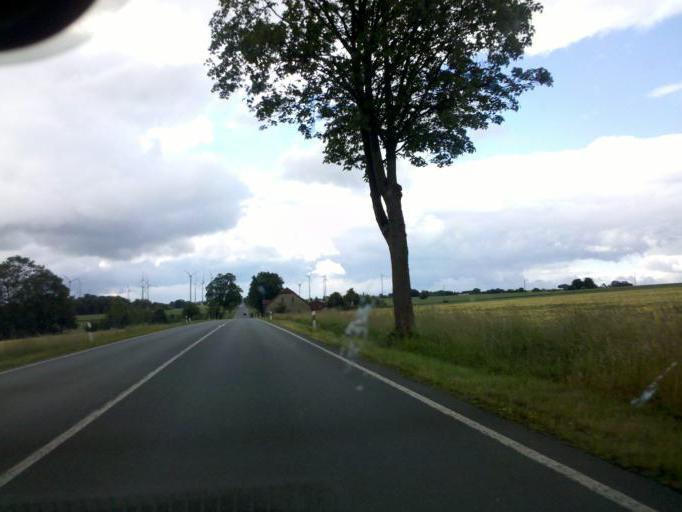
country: DE
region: North Rhine-Westphalia
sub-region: Regierungsbezirk Arnsberg
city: Anrochte
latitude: 51.5280
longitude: 8.3249
